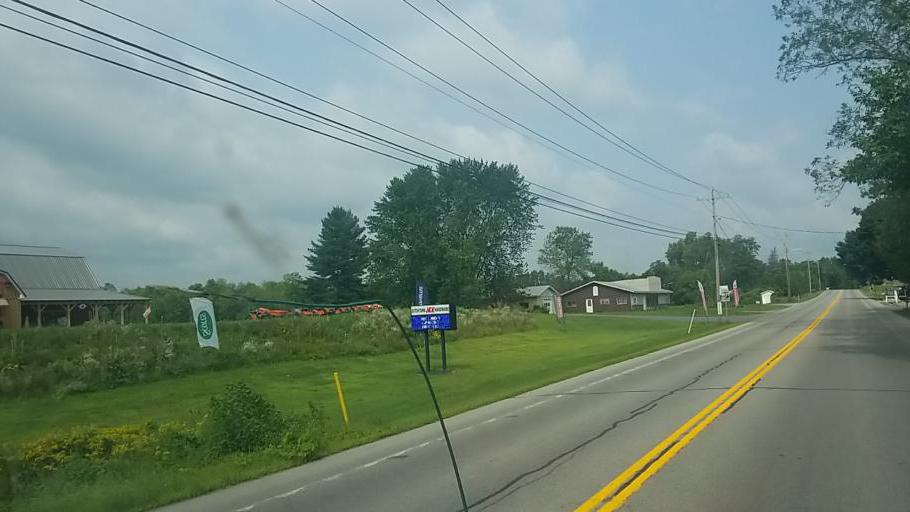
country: US
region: New York
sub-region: Montgomery County
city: Fort Plain
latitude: 42.9207
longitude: -74.5978
